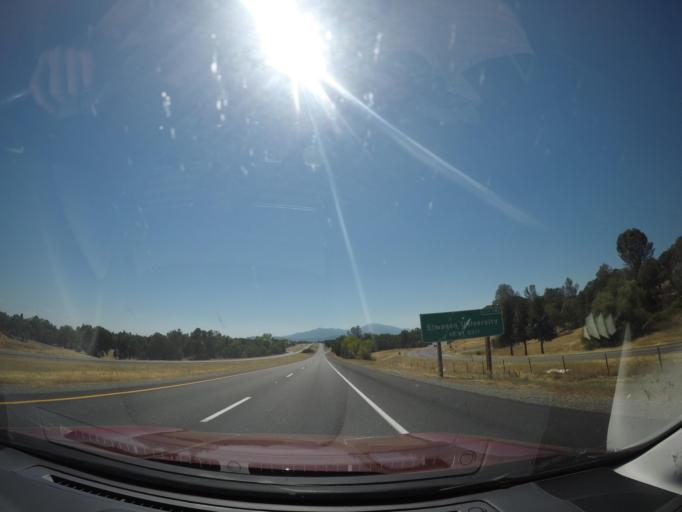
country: US
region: California
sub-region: Shasta County
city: Redding
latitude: 40.6162
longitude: -122.3426
